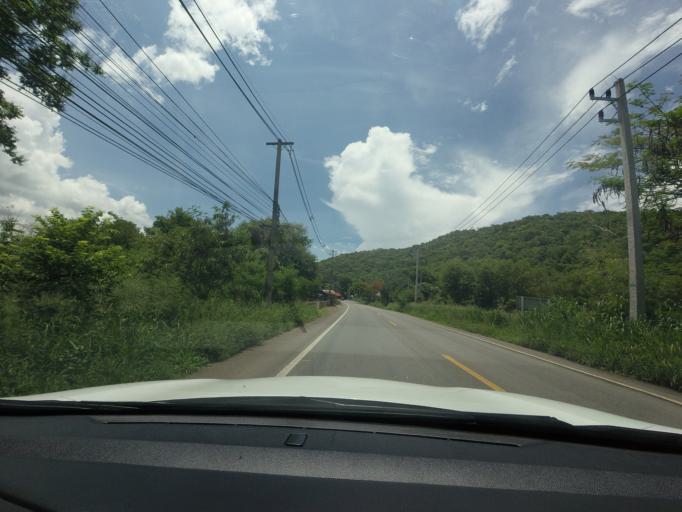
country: TH
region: Sara Buri
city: Muak Lek
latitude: 14.6202
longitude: 101.2123
